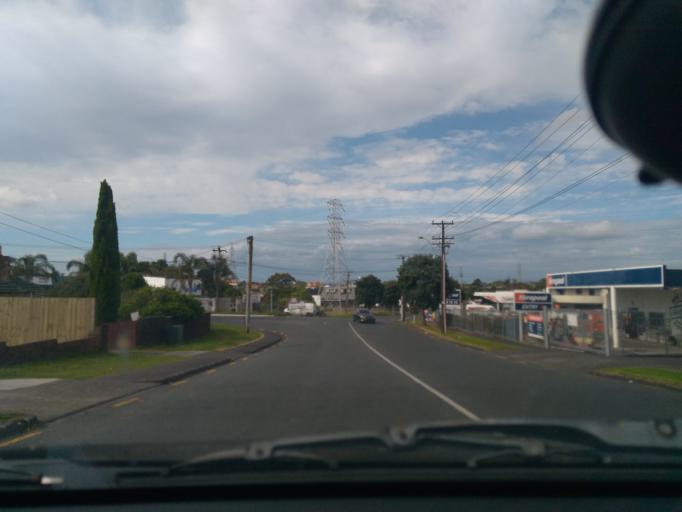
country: NZ
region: Auckland
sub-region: Auckland
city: Waitakere
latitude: -36.9040
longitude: 174.6843
